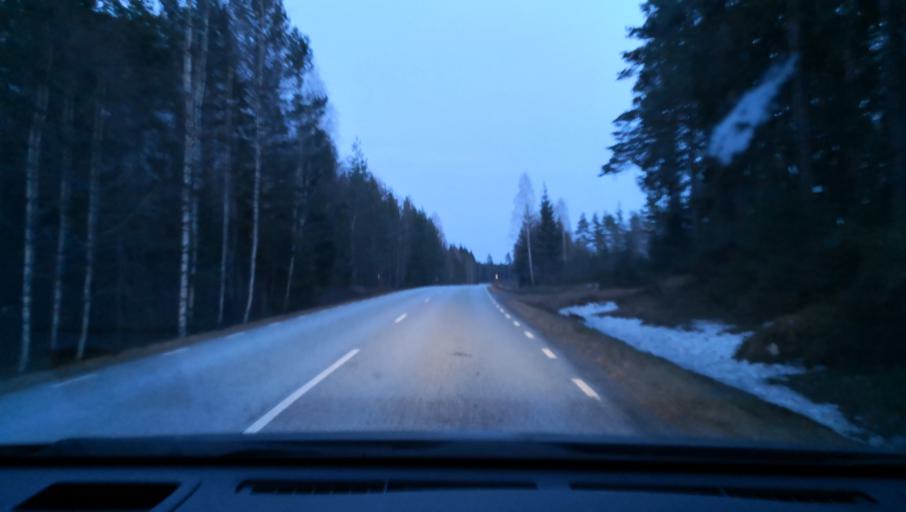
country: SE
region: OErebro
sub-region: Lindesbergs Kommun
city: Frovi
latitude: 59.5946
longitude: 15.3860
